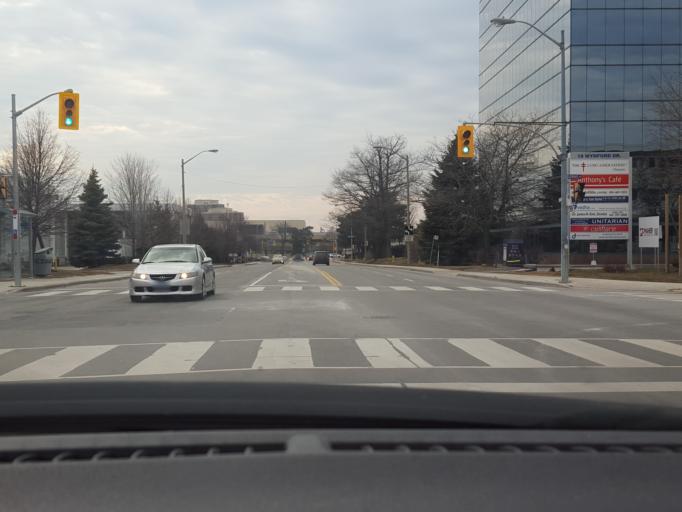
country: CA
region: Ontario
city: Willowdale
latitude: 43.7236
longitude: -79.3362
